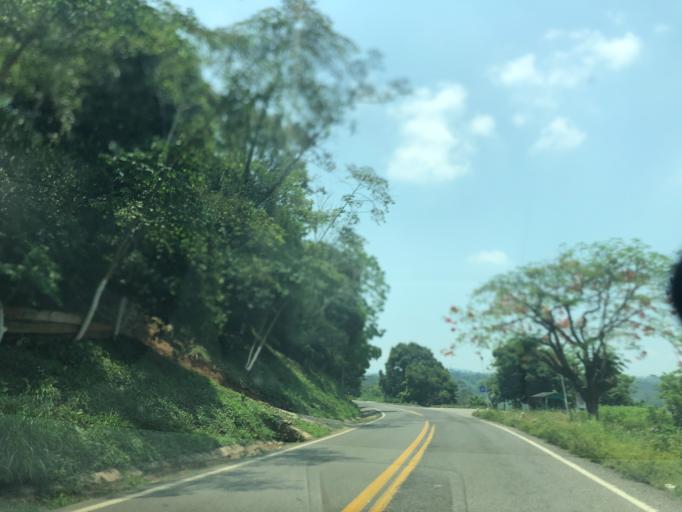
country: MX
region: Tabasco
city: Teapa
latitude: 17.5550
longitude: -92.9860
